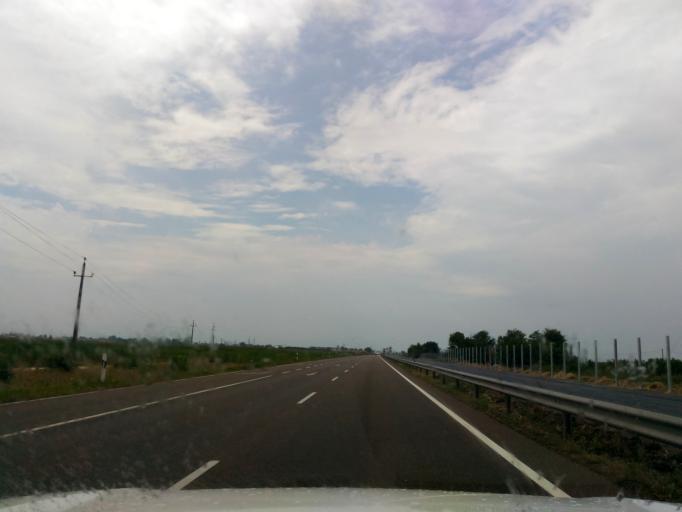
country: HU
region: Pest
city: Cegled
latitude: 47.1942
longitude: 19.8275
